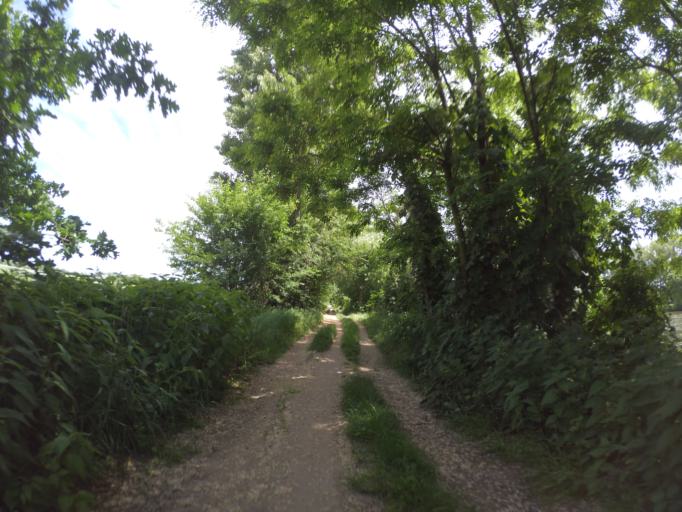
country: CZ
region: Central Bohemia
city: Lysa nad Labem
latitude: 50.1813
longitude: 14.8385
